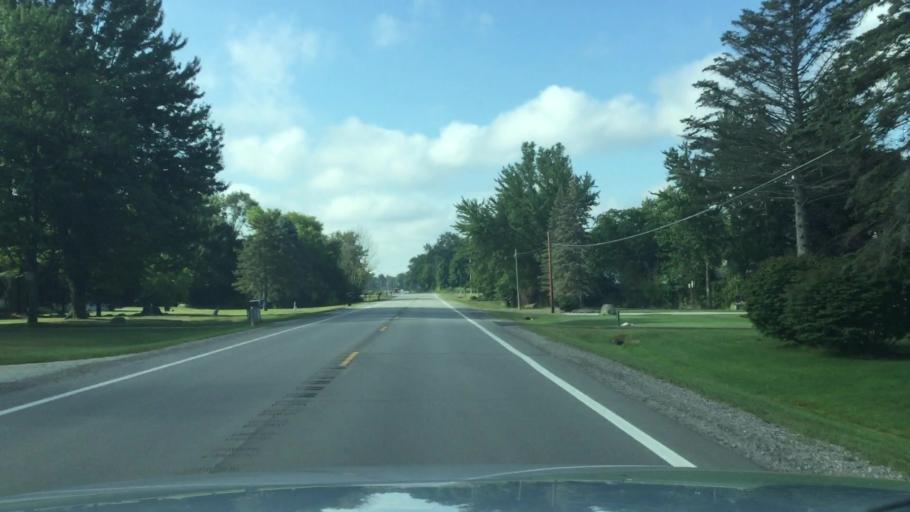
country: US
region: Michigan
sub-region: Genesee County
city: Clio
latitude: 43.2242
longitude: -83.7352
